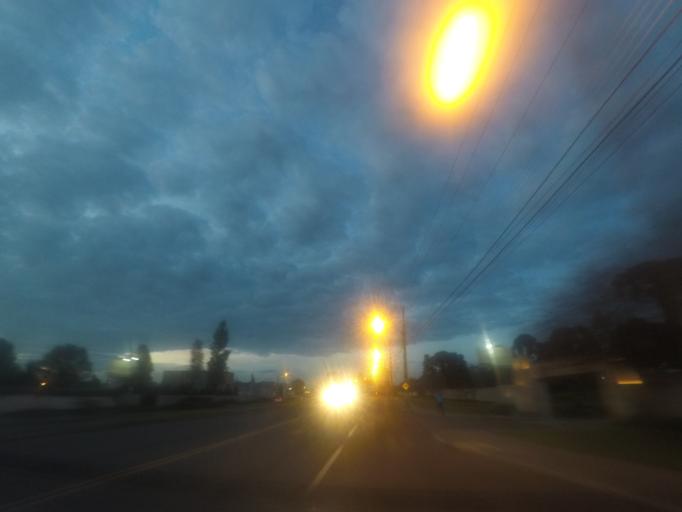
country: BR
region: Parana
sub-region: Pinhais
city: Pinhais
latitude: -25.3987
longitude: -49.1892
